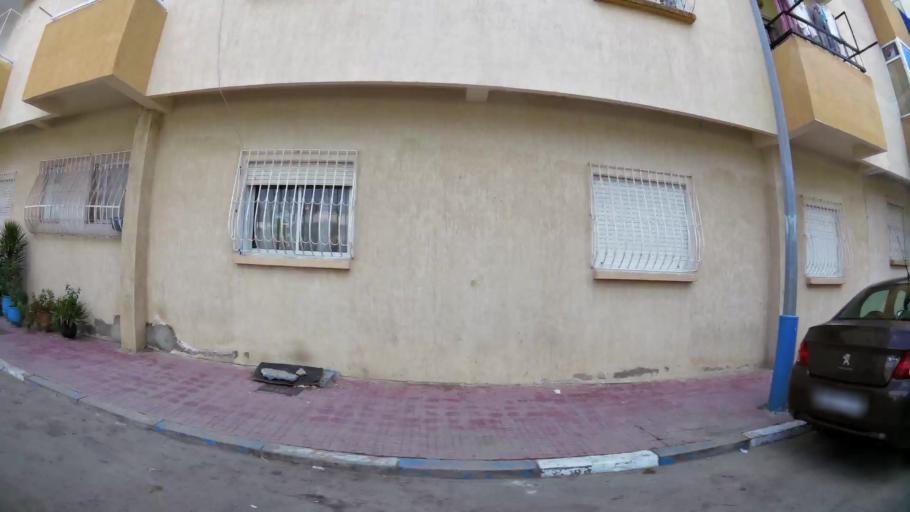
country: MA
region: Tanger-Tetouan
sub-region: Tanger-Assilah
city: Tangier
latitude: 35.7732
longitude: -5.8311
